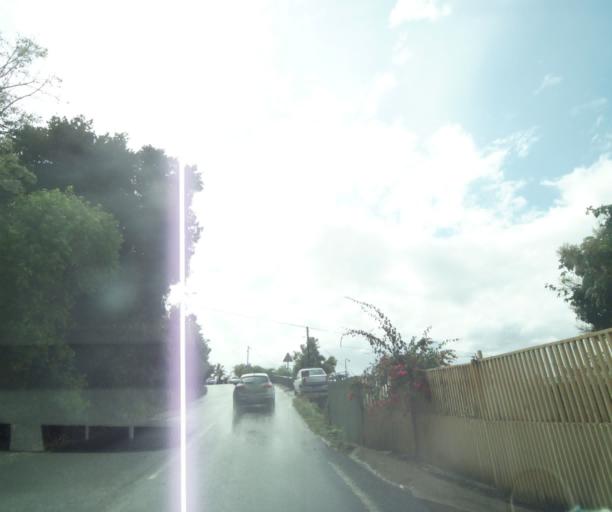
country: RE
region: Reunion
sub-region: Reunion
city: Saint-Paul
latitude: -20.9972
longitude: 55.3283
